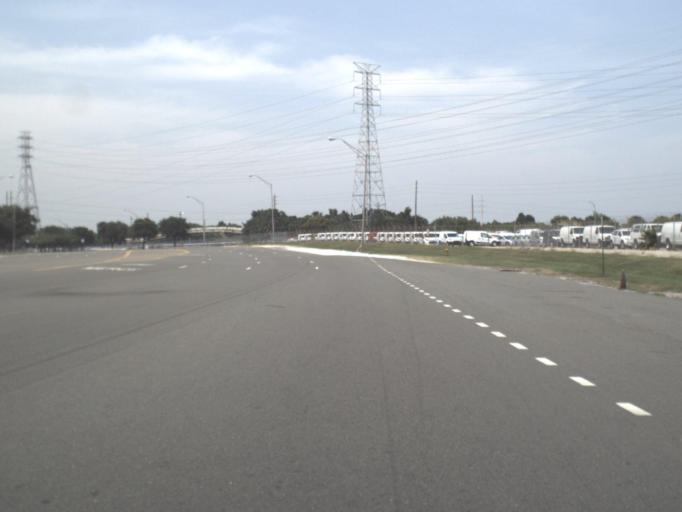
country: US
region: Florida
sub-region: Duval County
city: Jacksonville
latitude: 30.4035
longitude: -81.5370
